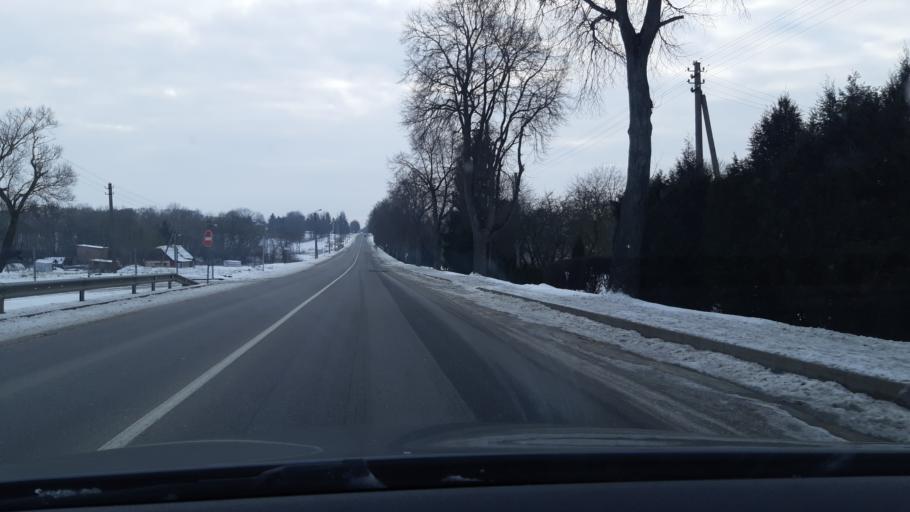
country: LT
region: Kauno apskritis
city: Kedainiai
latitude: 55.2441
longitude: 23.8353
